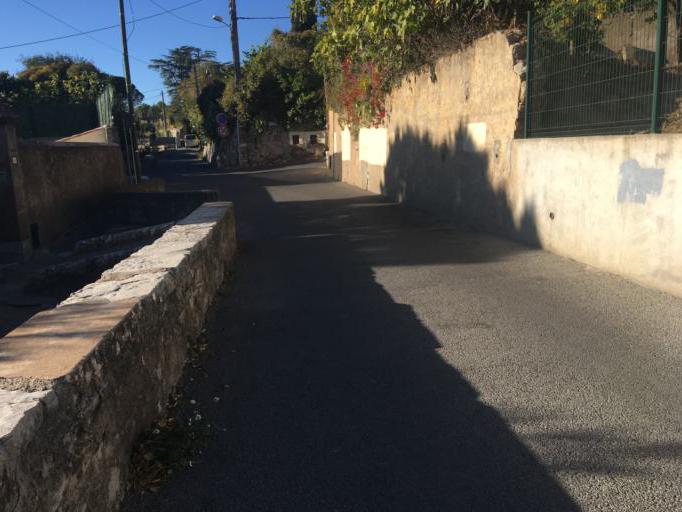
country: FR
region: Provence-Alpes-Cote d'Azur
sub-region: Departement du Var
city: Draguignan
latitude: 43.5429
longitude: 6.4632
